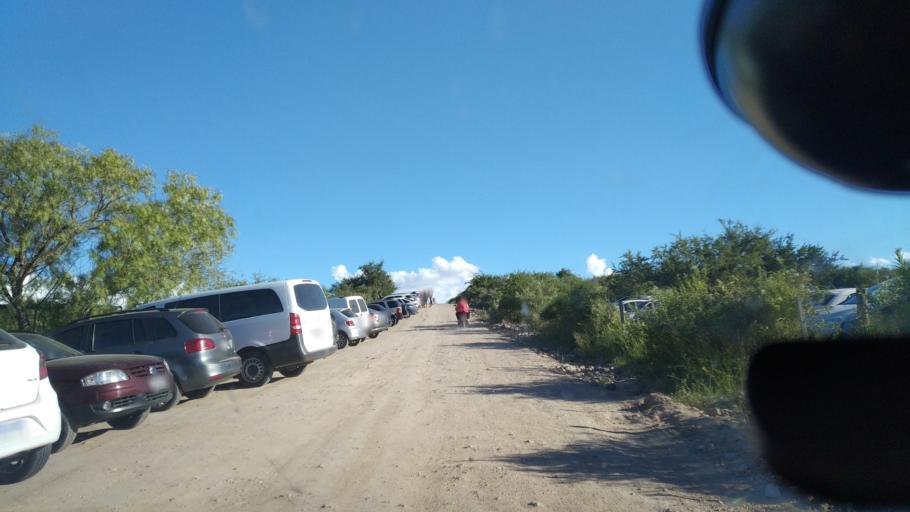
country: AR
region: Cordoba
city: Mina Clavero
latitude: -31.7263
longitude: -64.9932
